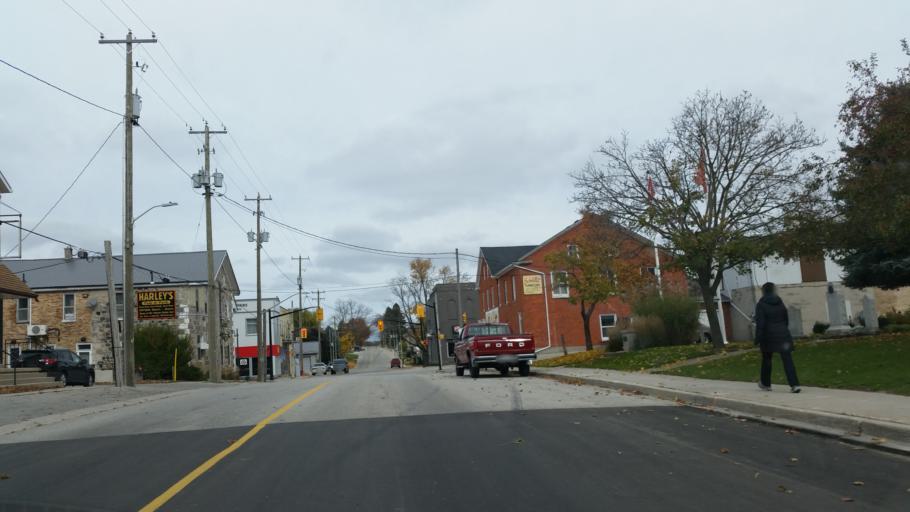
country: CA
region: Ontario
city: Hanover
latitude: 44.0416
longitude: -81.1196
